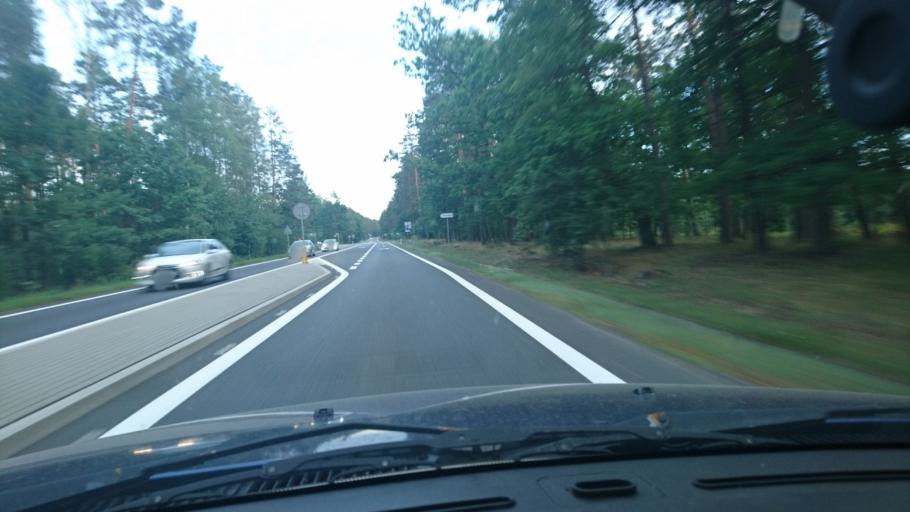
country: PL
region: Silesian Voivodeship
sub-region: Powiat lubliniecki
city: Lubliniec
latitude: 50.6067
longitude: 18.6970
